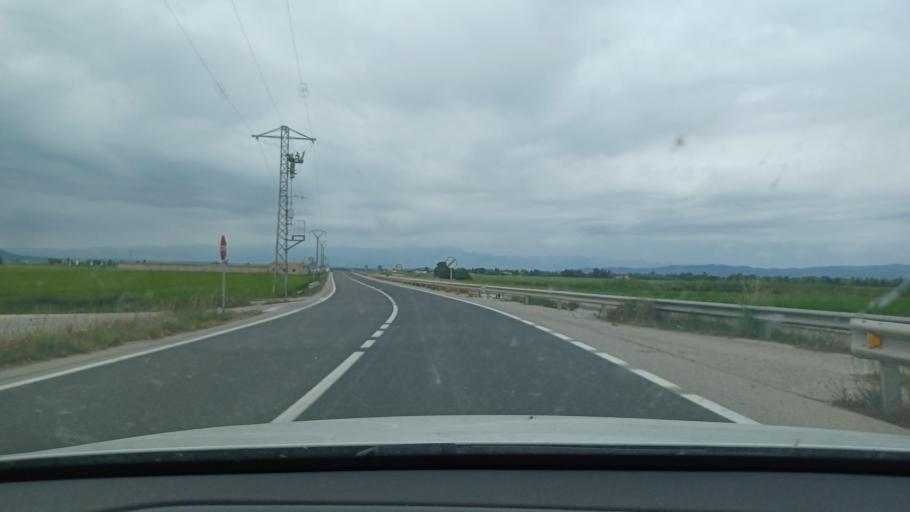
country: ES
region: Catalonia
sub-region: Provincia de Tarragona
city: Deltebre
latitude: 40.7060
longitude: 0.7046
